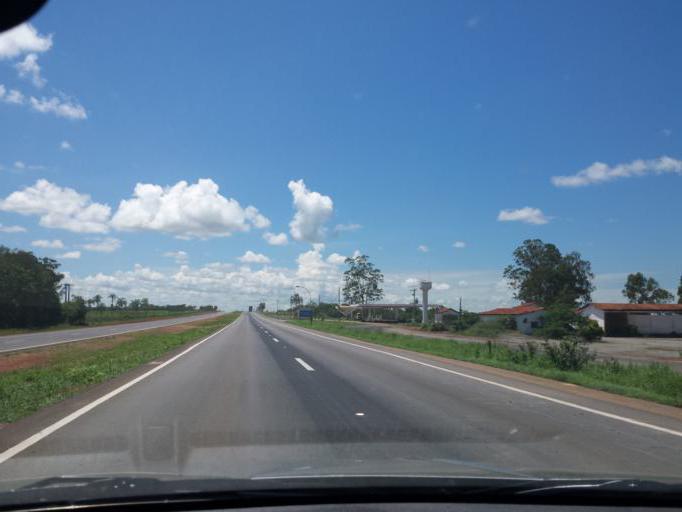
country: BR
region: Goias
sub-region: Luziania
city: Luziania
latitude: -16.4970
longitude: -47.8122
